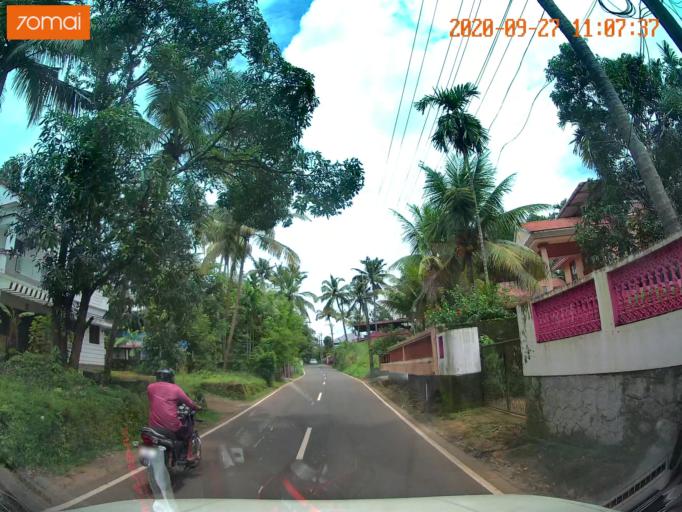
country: IN
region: Kerala
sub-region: Thrissur District
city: Irinjalakuda
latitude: 10.4284
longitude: 76.2363
